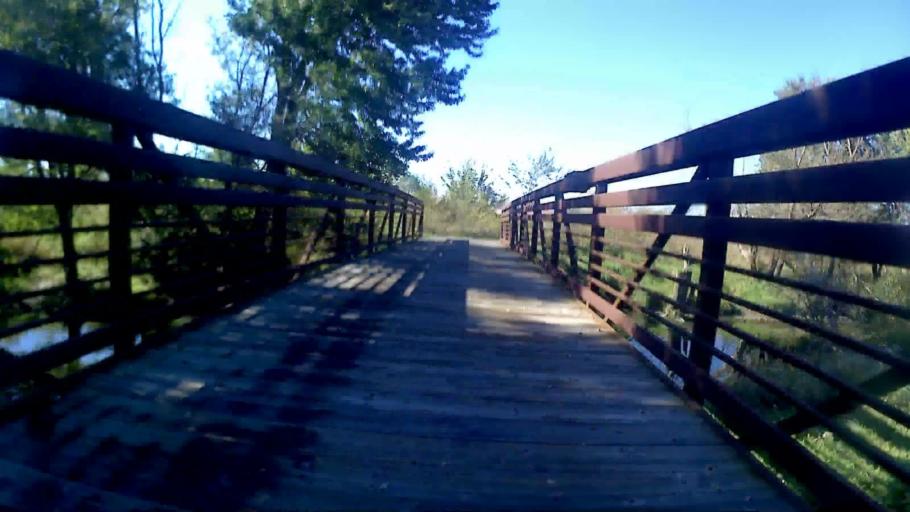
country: US
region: Illinois
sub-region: DuPage County
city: Itasca
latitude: 41.9824
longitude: -87.9909
